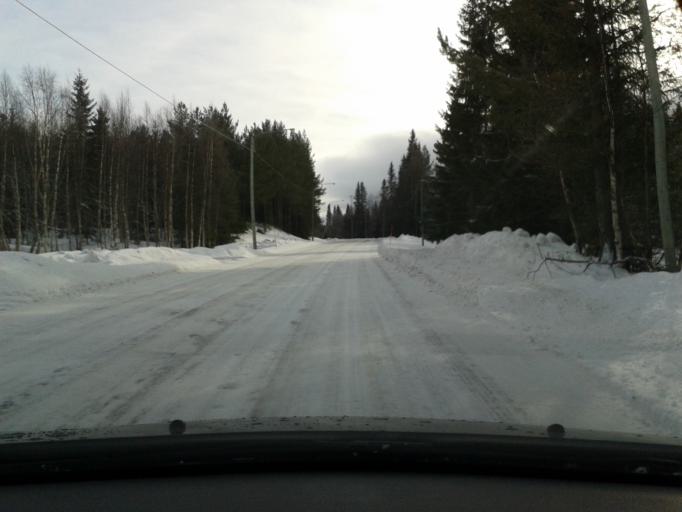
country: SE
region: Vaesterbotten
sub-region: Vilhelmina Kommun
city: Sjoberg
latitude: 64.6891
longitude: 16.2730
